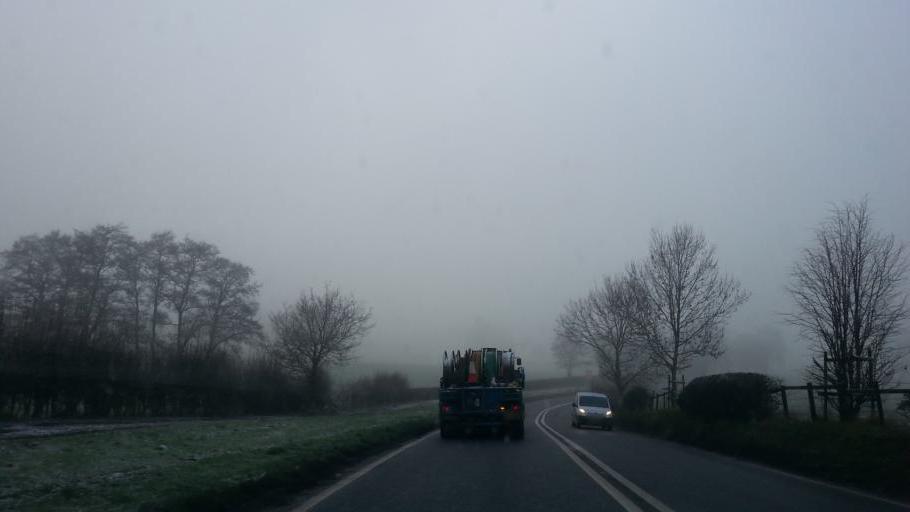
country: GB
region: England
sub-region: Cheshire East
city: Siddington
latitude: 53.2200
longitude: -2.2364
